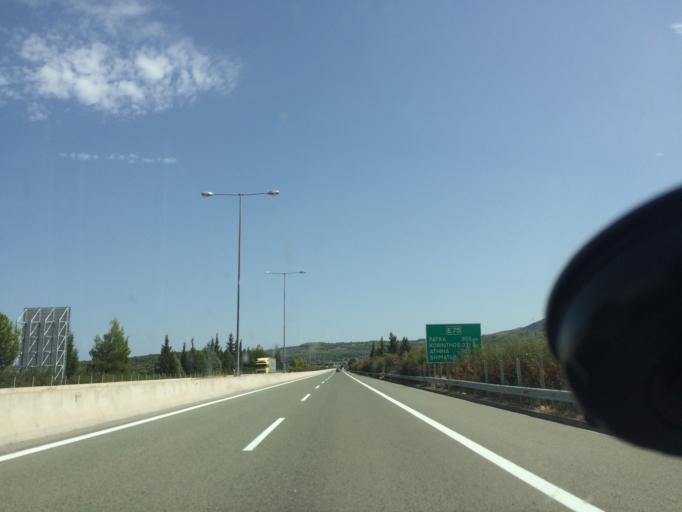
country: GR
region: Central Greece
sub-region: Nomos Fthiotidos
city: Martinon
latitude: 38.6203
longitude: 23.1323
